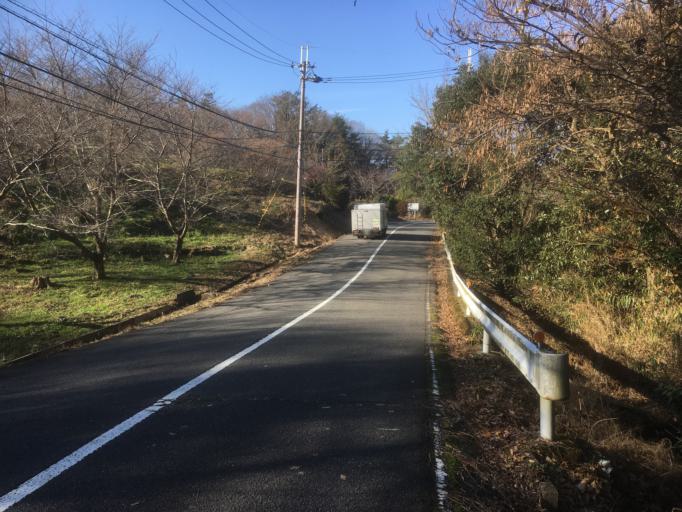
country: JP
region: Nara
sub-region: Ikoma-shi
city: Ikoma
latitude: 34.6949
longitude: 135.6748
